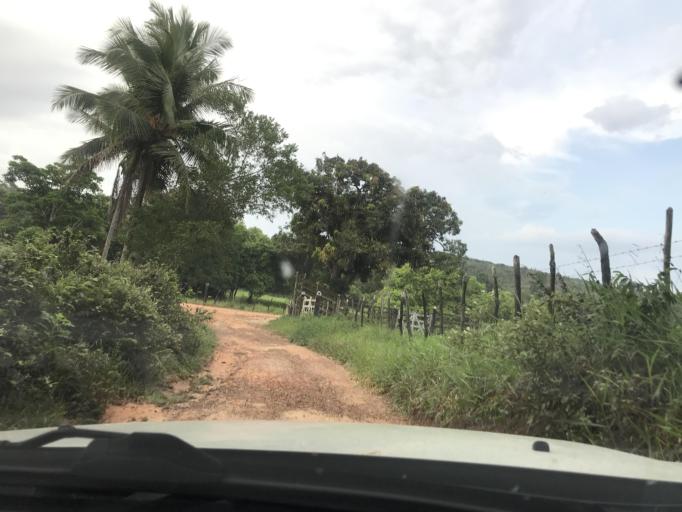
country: BR
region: Bahia
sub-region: Entre Rios
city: Entre Rios
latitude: -12.0123
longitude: -38.2201
